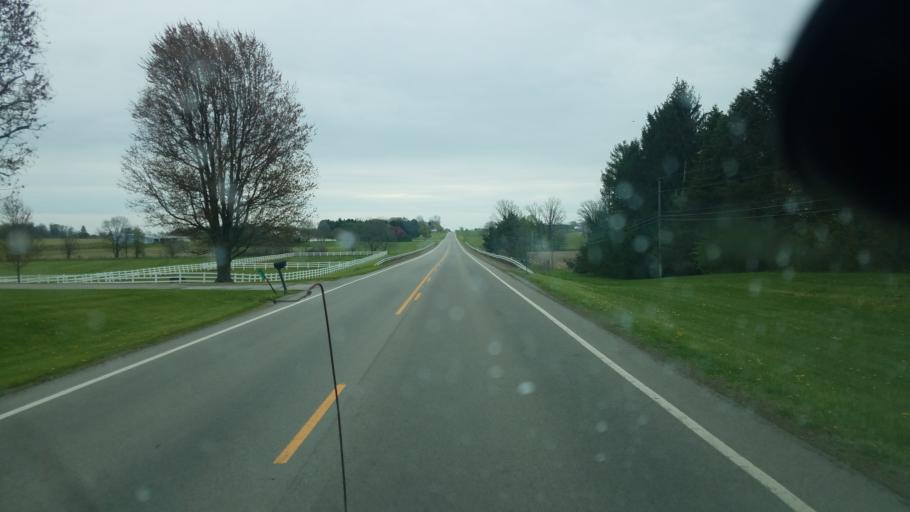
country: US
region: Ohio
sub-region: Hardin County
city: Kenton
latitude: 40.6438
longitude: -83.5600
